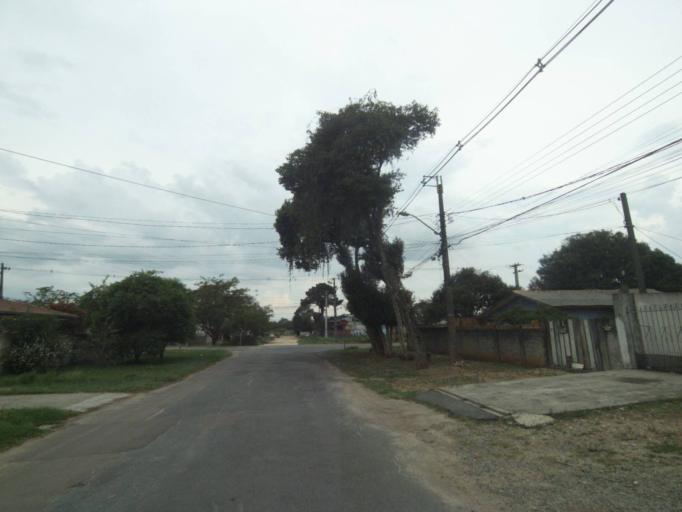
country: BR
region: Parana
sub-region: Pinhais
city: Pinhais
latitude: -25.4149
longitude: -49.1987
